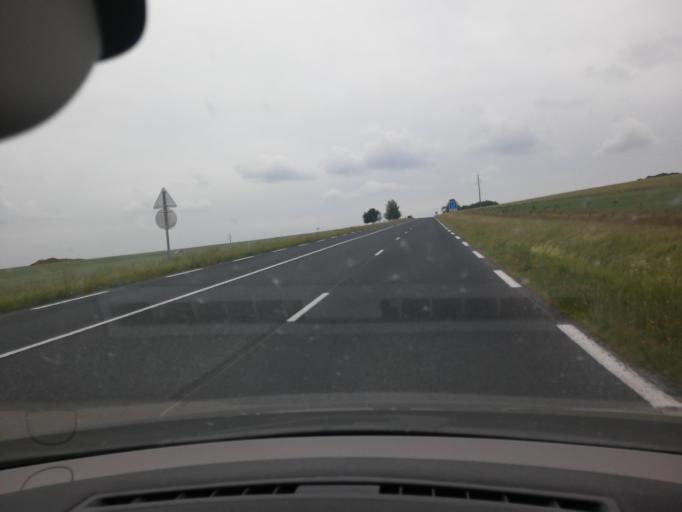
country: FR
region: Lorraine
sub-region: Departement de la Meuse
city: Saint-Mihiel
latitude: 48.8728
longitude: 5.5210
